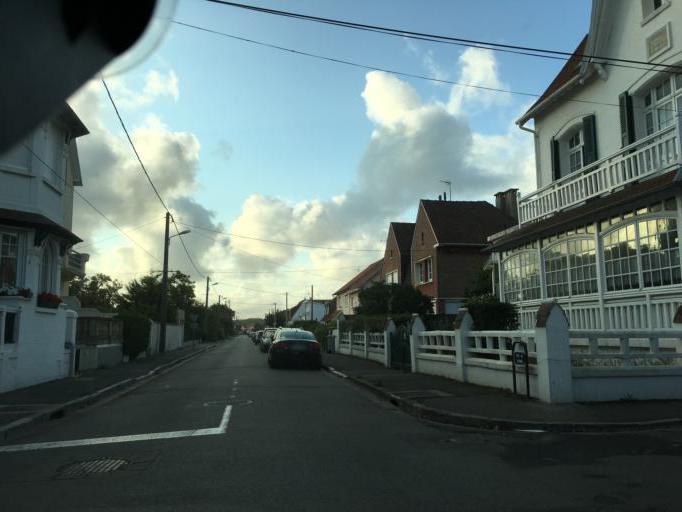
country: FR
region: Nord-Pas-de-Calais
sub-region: Departement du Pas-de-Calais
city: Berck-Plage
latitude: 50.4012
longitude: 1.5651
